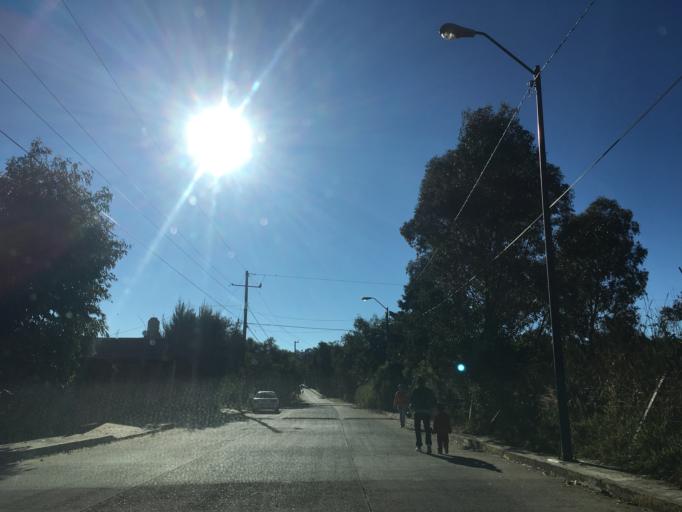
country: MX
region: Michoacan
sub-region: Morelia
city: Montana Monarca (Punta Altozano)
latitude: 19.6547
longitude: -101.1513
